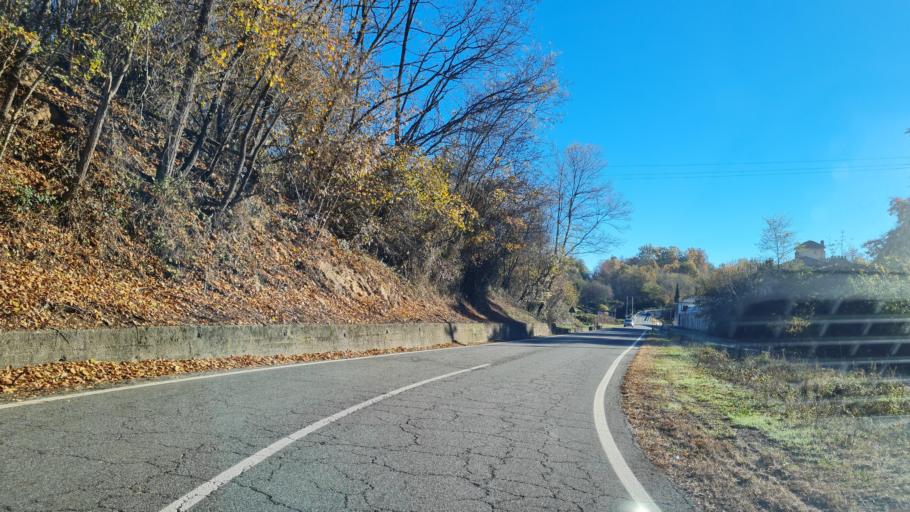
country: IT
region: Piedmont
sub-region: Provincia di Biella
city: Masserano
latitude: 45.5951
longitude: 8.2320
